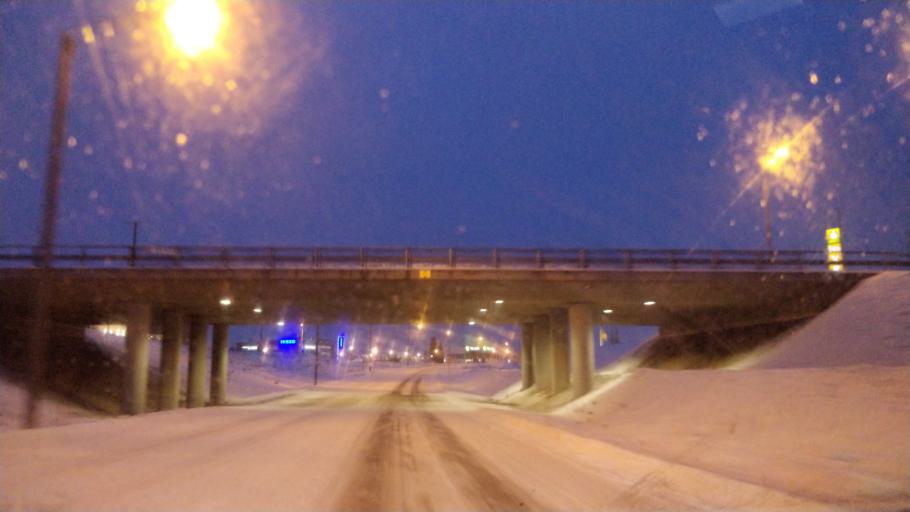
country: FI
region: Northern Ostrobothnia
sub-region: Oulu
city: Kempele
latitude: 64.8641
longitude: 25.5175
